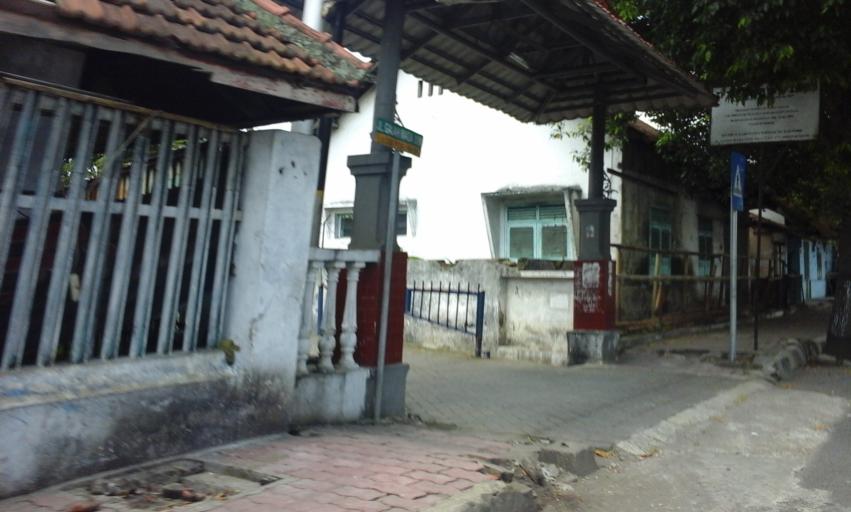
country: ID
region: East Java
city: Kaliwates
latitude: -8.1776
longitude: 113.6810
